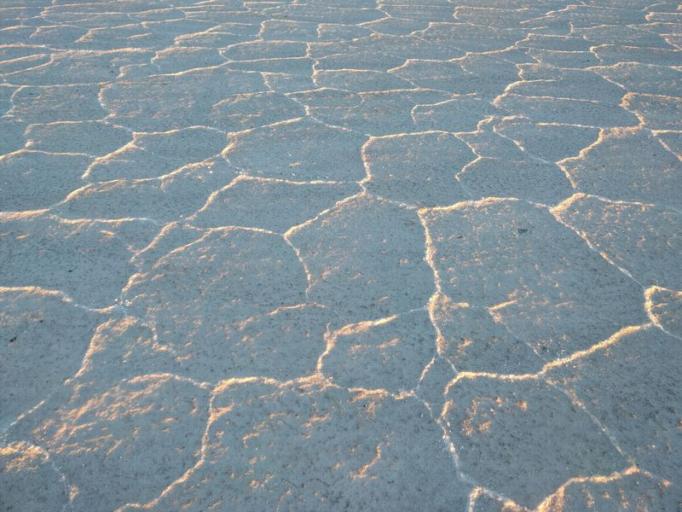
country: BO
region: Potosi
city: Colchani
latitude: -20.2405
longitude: -67.6279
